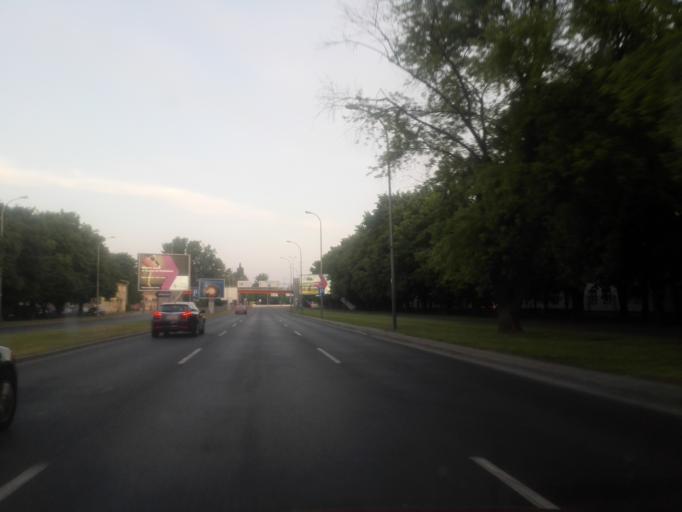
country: PL
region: Masovian Voivodeship
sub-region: Warszawa
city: Wlochy
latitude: 52.1764
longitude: 20.9789
